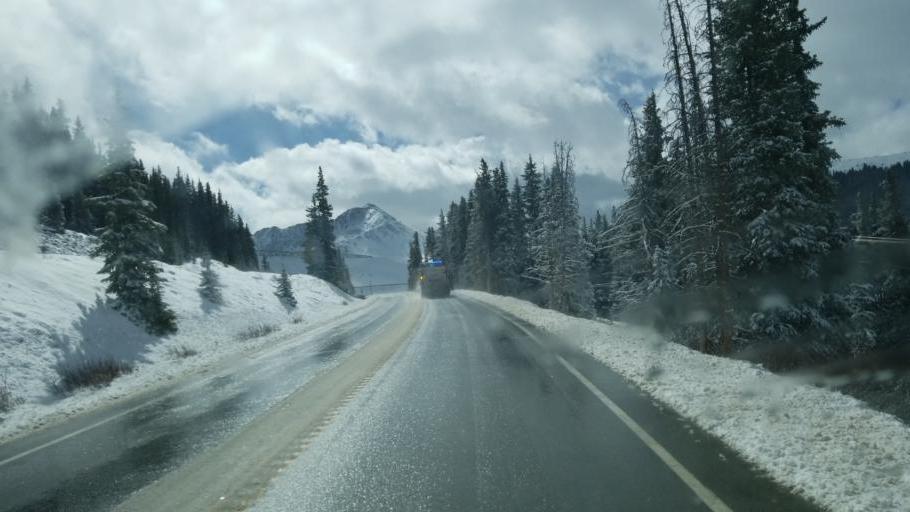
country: US
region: Colorado
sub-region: Lake County
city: Leadville
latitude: 39.3873
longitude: -106.1916
